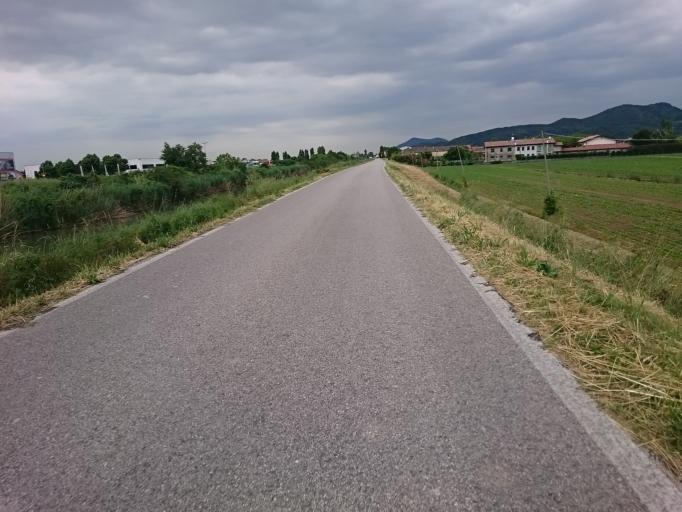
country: IT
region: Veneto
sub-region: Provincia di Padova
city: Terradura
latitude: 45.3288
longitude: 11.8154
